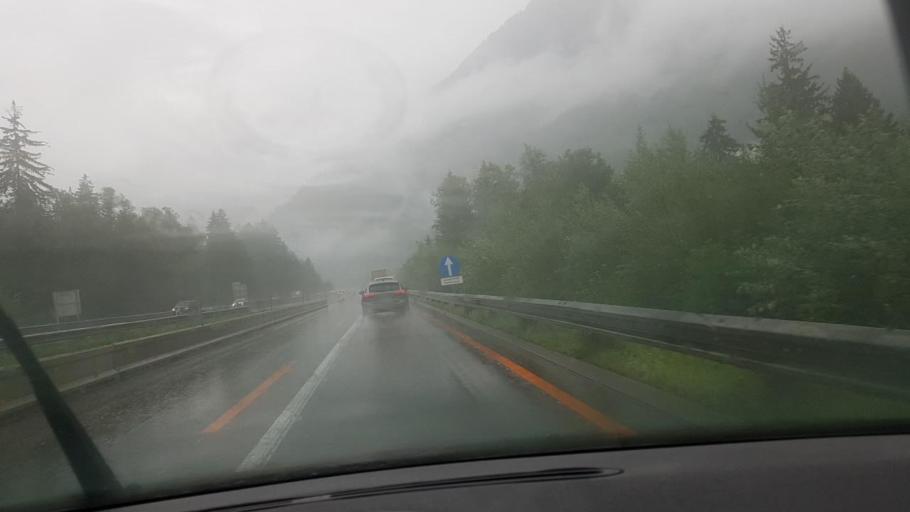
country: AT
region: Vorarlberg
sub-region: Politischer Bezirk Bludenz
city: Nenzing
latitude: 47.1869
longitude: 9.7216
